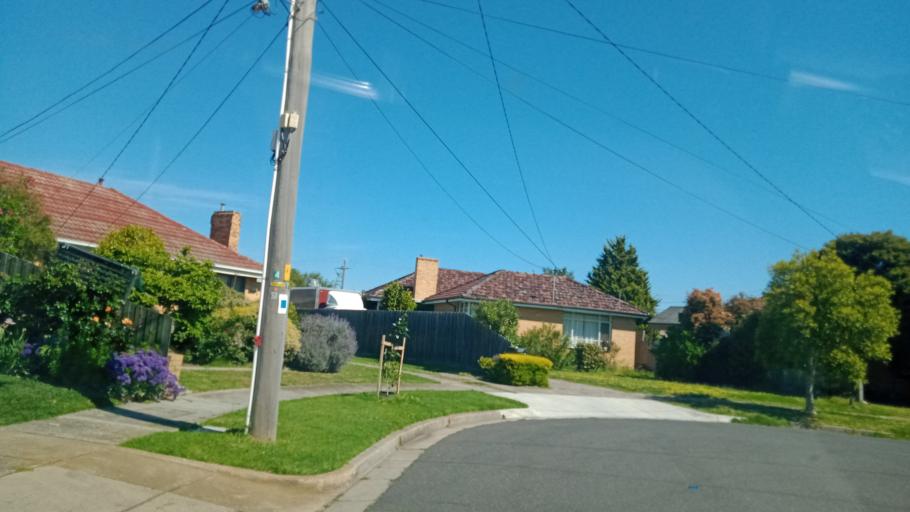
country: AU
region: Victoria
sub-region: Monash
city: Oakleigh South
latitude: -37.9369
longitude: 145.0741
